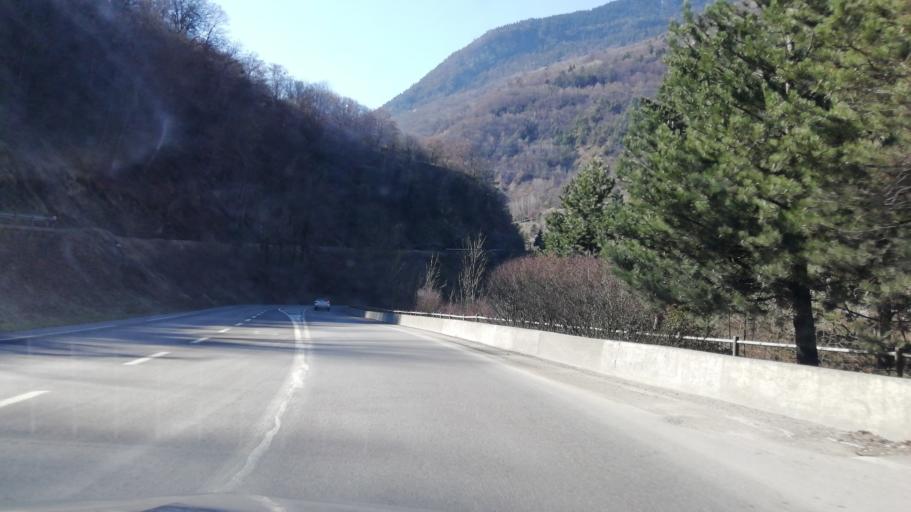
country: FR
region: Rhone-Alpes
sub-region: Departement de la Savoie
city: Salins-les-Thermes
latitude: 45.4658
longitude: 6.5305
